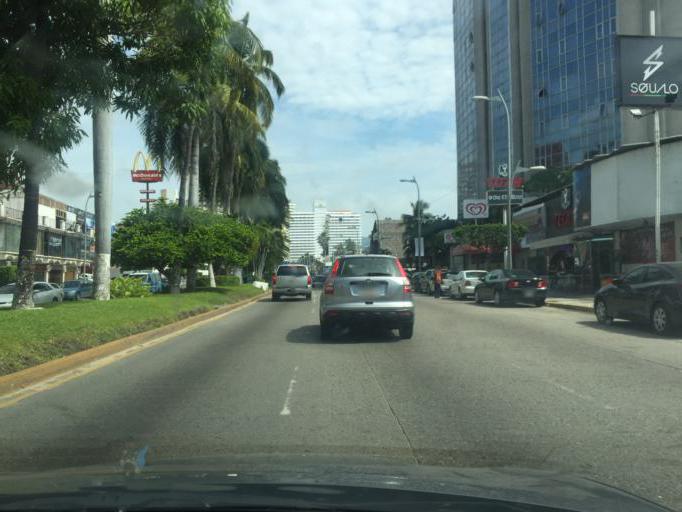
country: MX
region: Guerrero
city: Acapulco de Juarez
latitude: 16.8586
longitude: -99.8715
